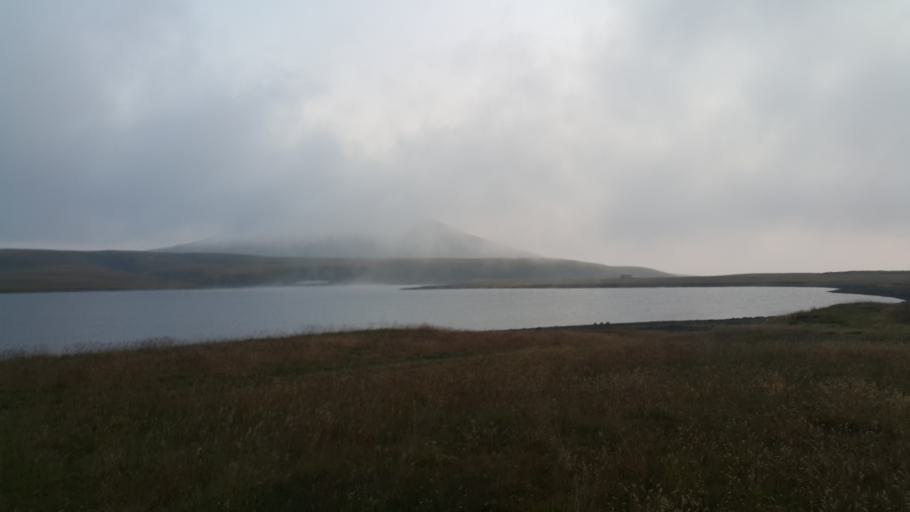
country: AM
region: Geghark'unik'i Marz
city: Gandzak
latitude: 40.2863
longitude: 44.9221
